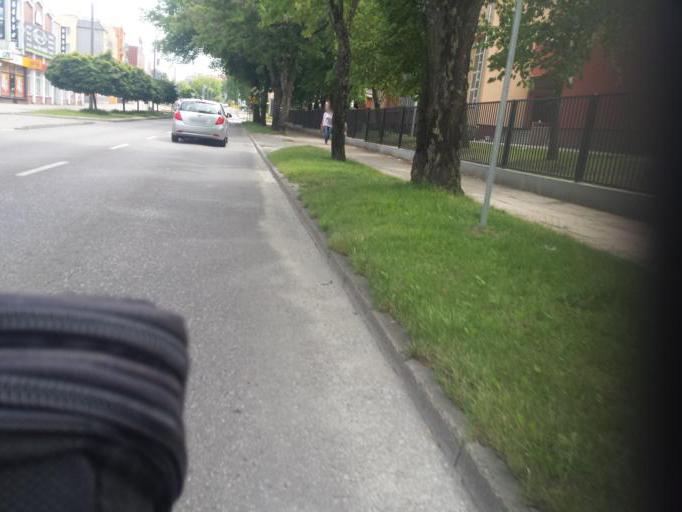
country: PL
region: Warmian-Masurian Voivodeship
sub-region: Powiat ilawski
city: Ilawa
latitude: 53.5904
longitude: 19.5651
